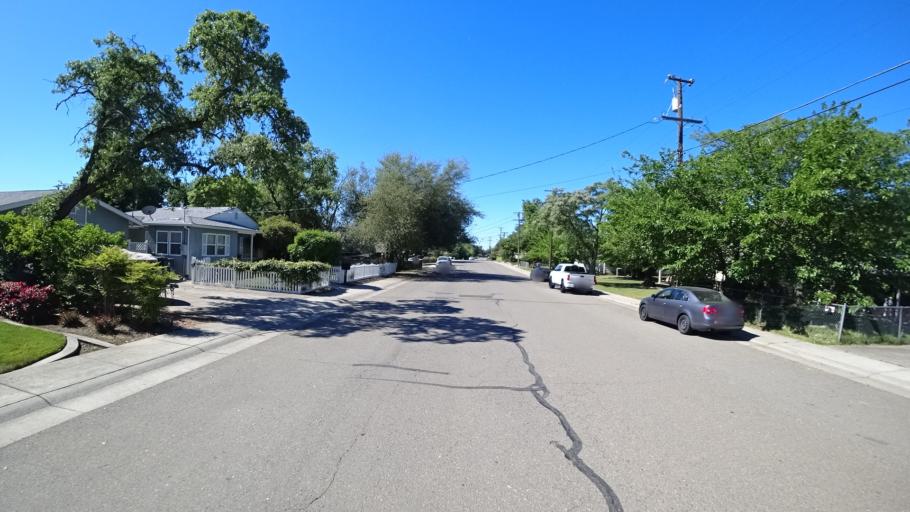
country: US
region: California
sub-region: Placer County
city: Rocklin
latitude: 38.7908
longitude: -121.2418
